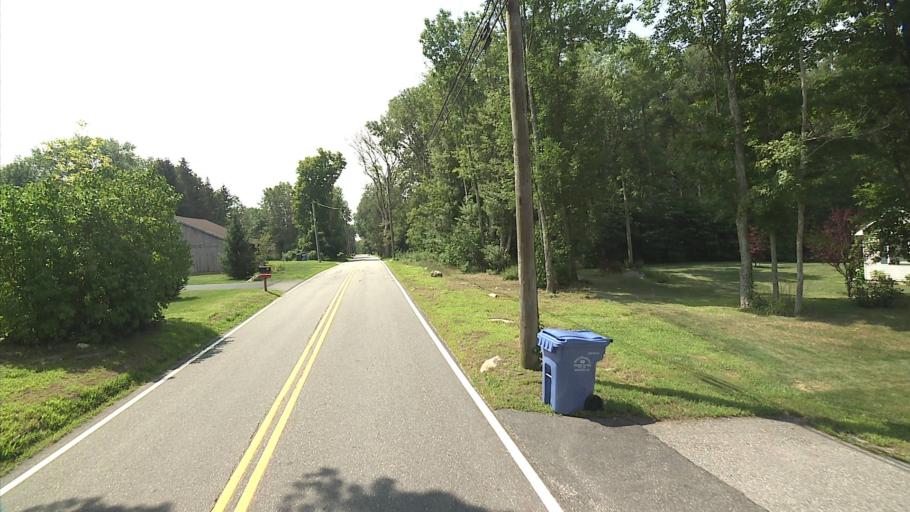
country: US
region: Connecticut
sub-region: Windham County
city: Danielson
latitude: 41.7872
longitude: -71.8339
